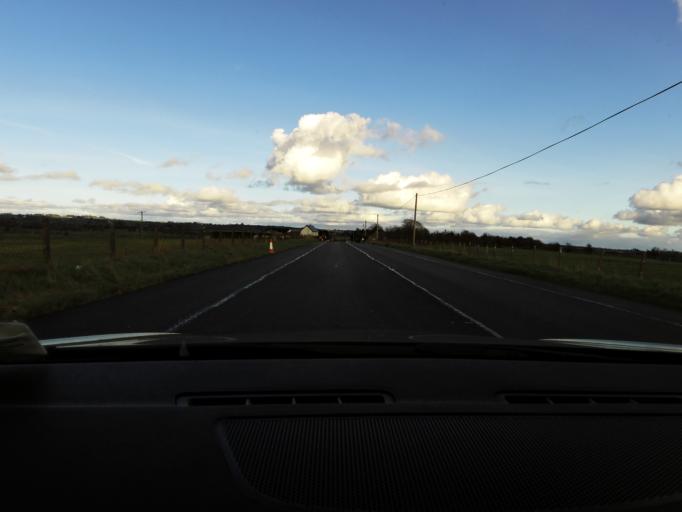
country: IE
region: Connaught
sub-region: Roscommon
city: Castlerea
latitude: 53.6904
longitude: -8.4221
